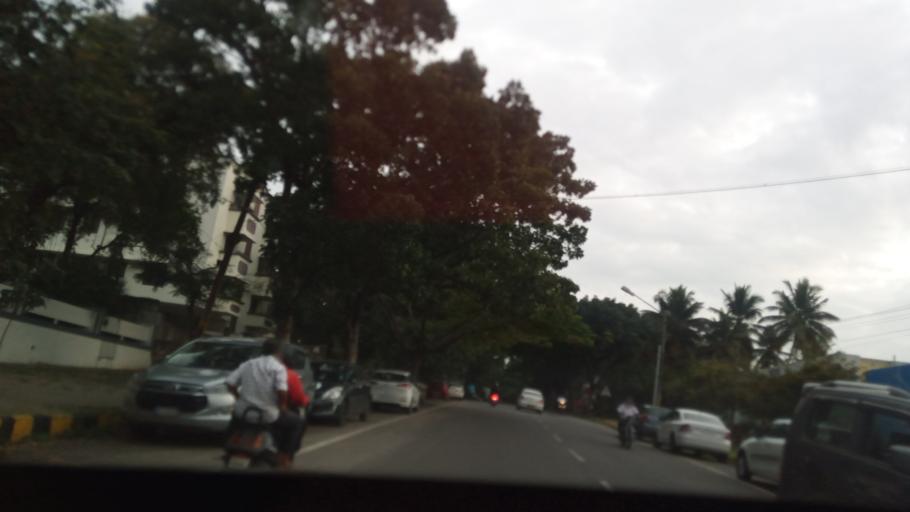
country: IN
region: Karnataka
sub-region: Mysore
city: Mysore
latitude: 12.3290
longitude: 76.6303
